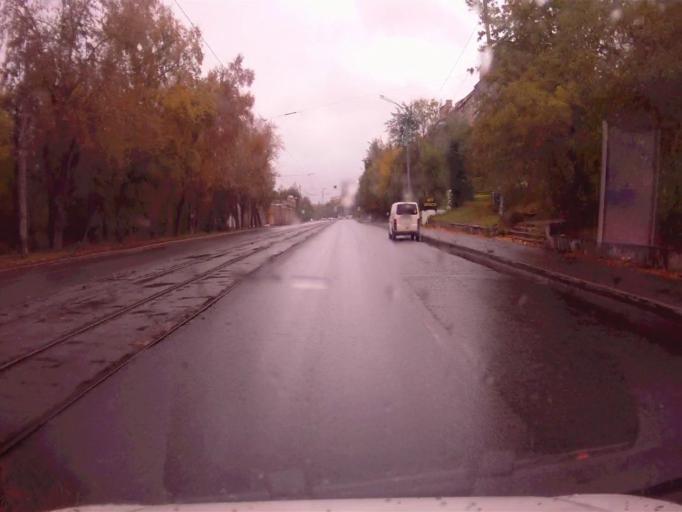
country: RU
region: Chelyabinsk
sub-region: Gorod Chelyabinsk
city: Chelyabinsk
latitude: 55.1816
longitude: 61.4146
